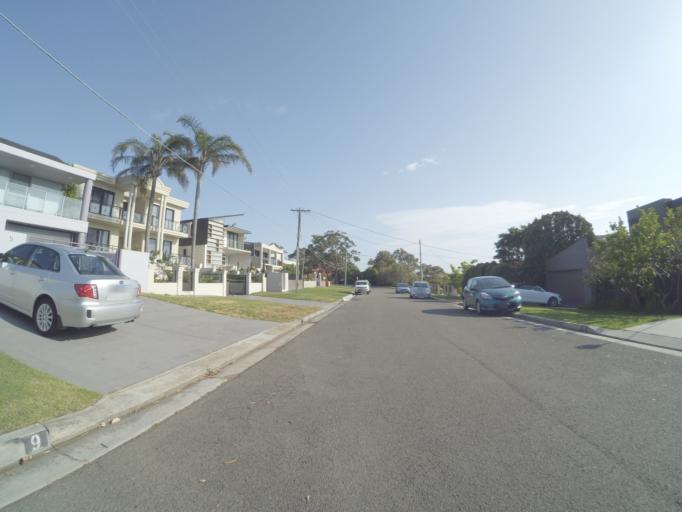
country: AU
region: New South Wales
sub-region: Sutherland Shire
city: Cronulla
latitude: -34.0721
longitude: 151.1393
